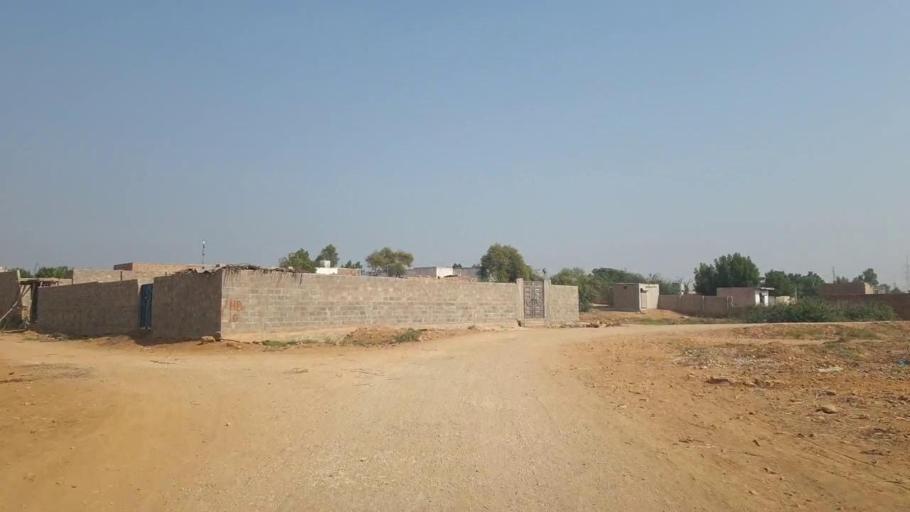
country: PK
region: Sindh
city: Jamshoro
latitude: 25.4620
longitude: 68.2896
